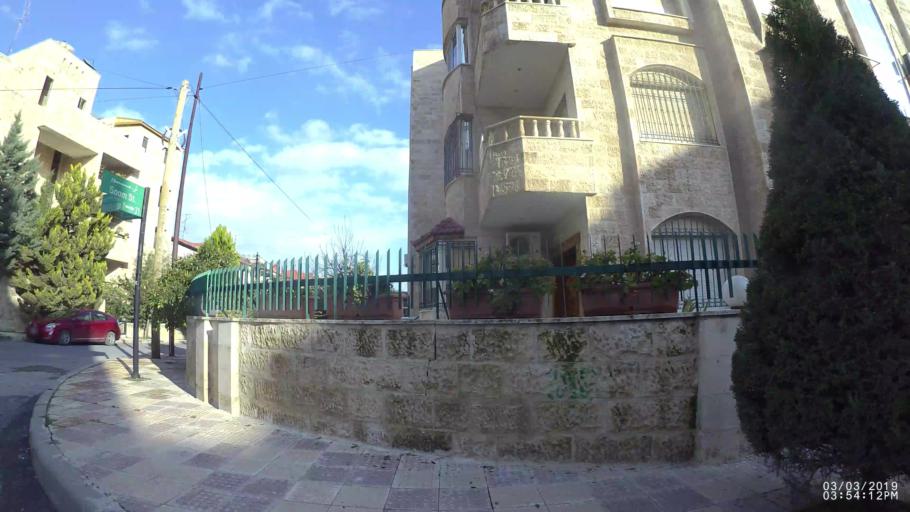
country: JO
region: Amman
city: Al Jubayhah
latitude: 31.9817
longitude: 35.8711
